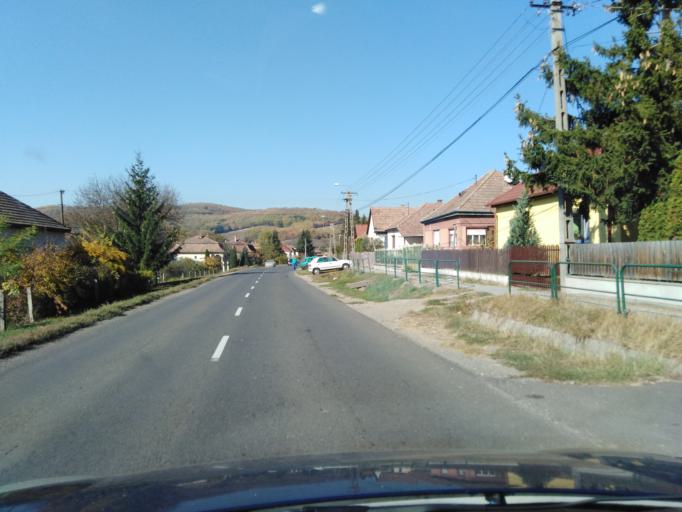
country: HU
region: Nograd
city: Karancslapujto
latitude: 48.1298
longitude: 19.7551
